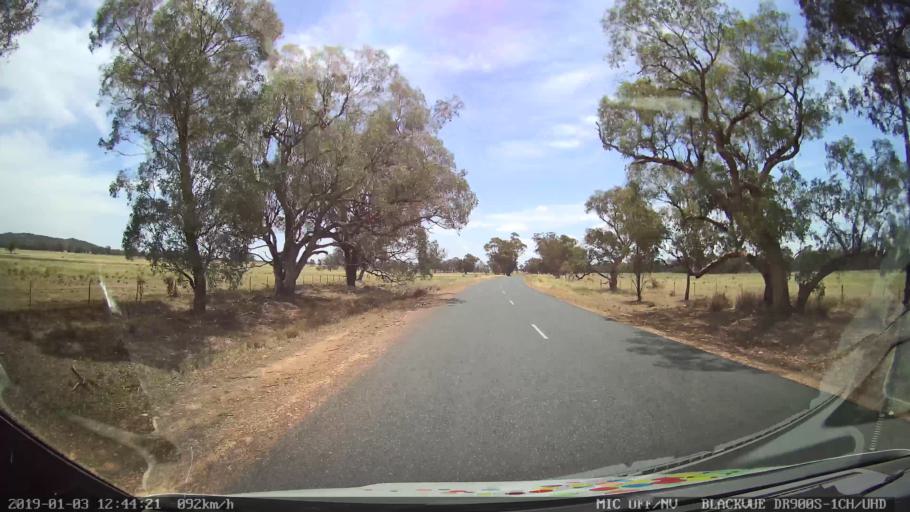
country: AU
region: New South Wales
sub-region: Weddin
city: Grenfell
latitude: -33.7625
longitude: 148.2152
